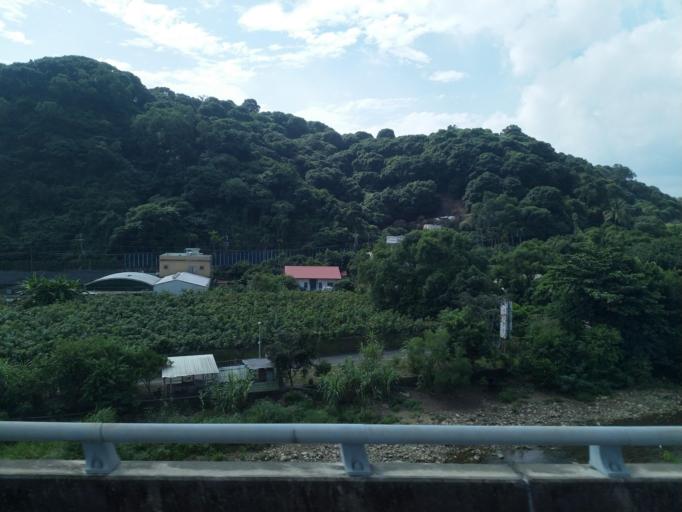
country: TW
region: Taiwan
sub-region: Pingtung
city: Pingtung
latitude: 22.7975
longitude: 120.4559
